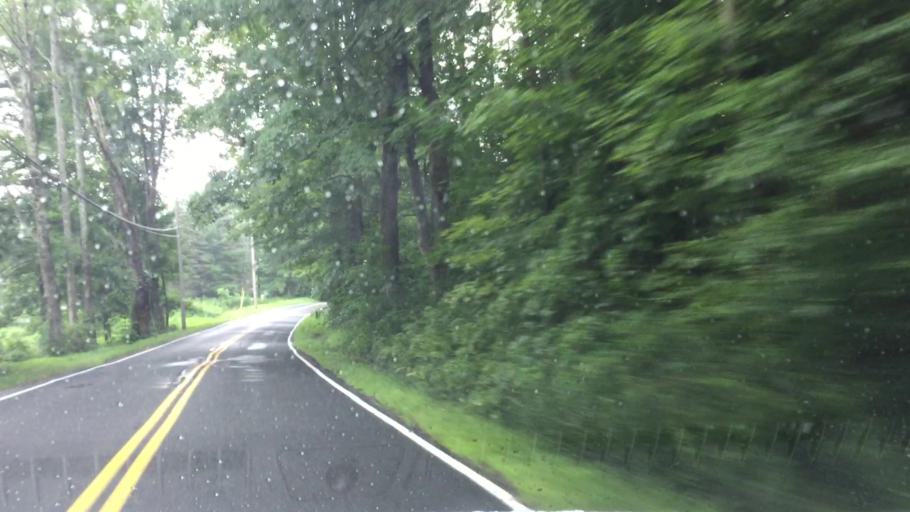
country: US
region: Massachusetts
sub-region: Berkshire County
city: Housatonic
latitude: 42.2943
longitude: -73.3850
